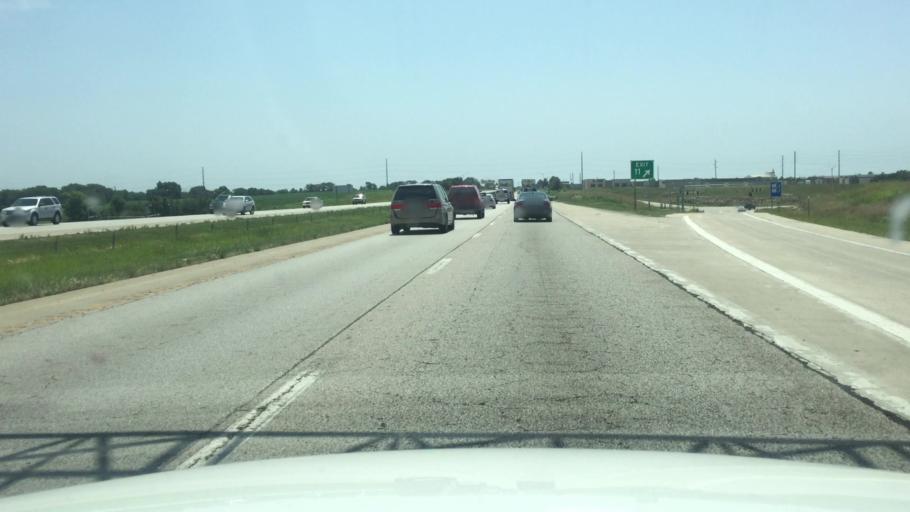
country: US
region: Missouri
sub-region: Jackson County
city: Lees Summit
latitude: 38.9708
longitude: -94.3580
